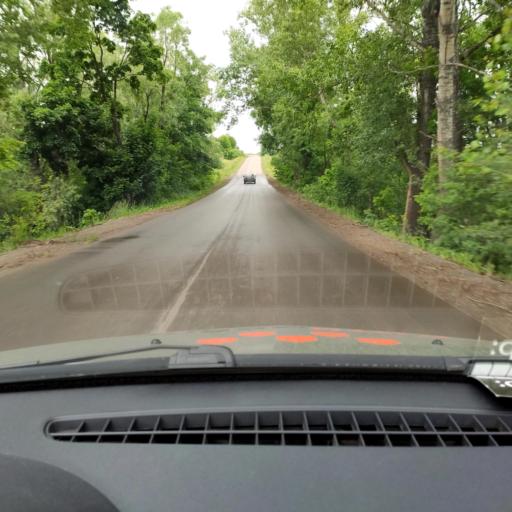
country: RU
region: Bashkortostan
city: Iglino
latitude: 54.8981
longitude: 56.2729
